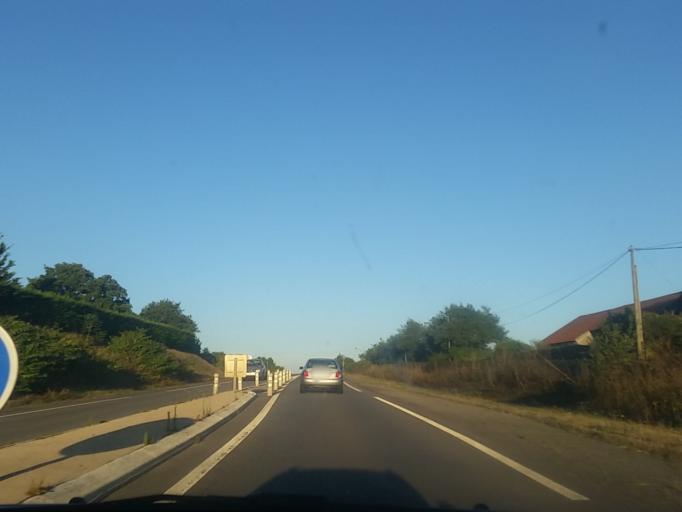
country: FR
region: Pays de la Loire
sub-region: Departement de la Loire-Atlantique
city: Rouans
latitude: 47.1890
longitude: -1.8267
